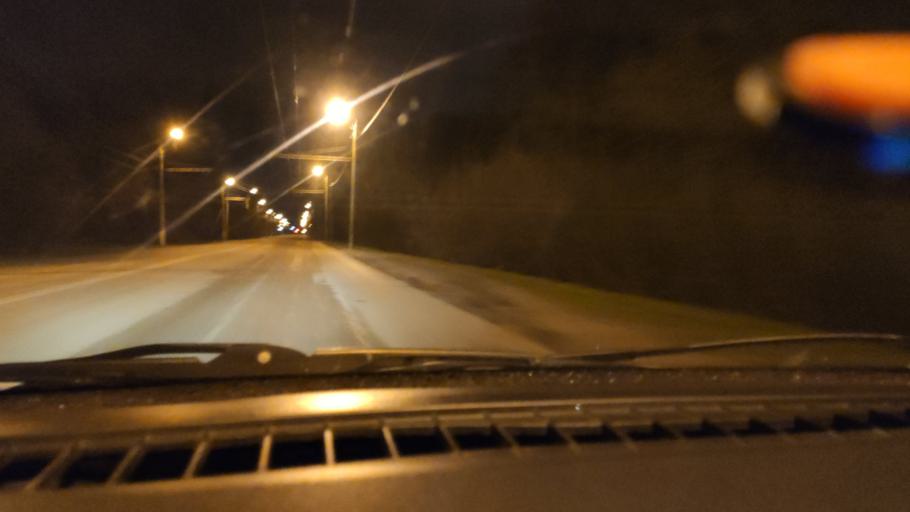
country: RU
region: Bashkortostan
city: Sterlitamak
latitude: 53.6568
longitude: 55.9211
